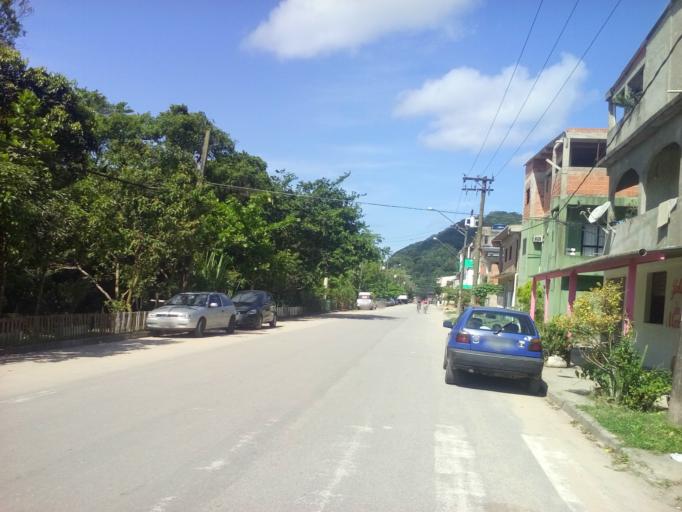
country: BR
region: Sao Paulo
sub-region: Guaruja
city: Guaruja
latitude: -23.9590
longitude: -46.2498
